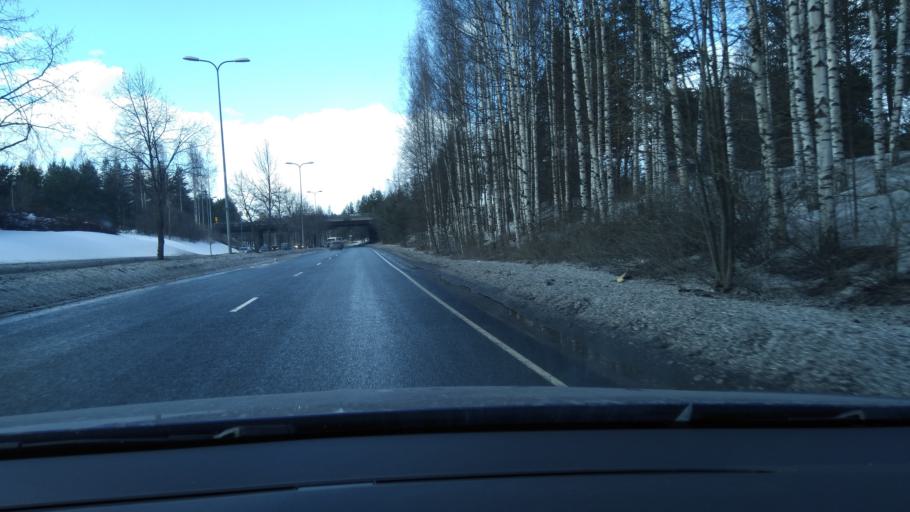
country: FI
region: Pirkanmaa
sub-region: Tampere
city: Tampere
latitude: 61.5009
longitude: 23.8077
